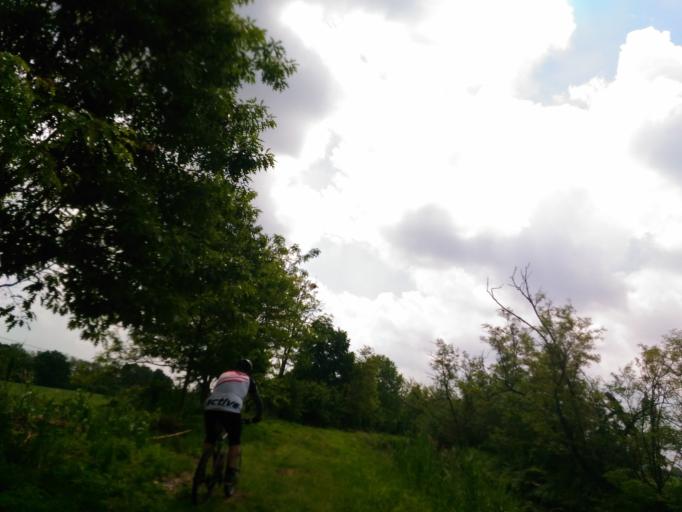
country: IT
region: Lombardy
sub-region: Provincia di Lodi
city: Turano Lodigiano
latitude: 45.2533
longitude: 9.6029
